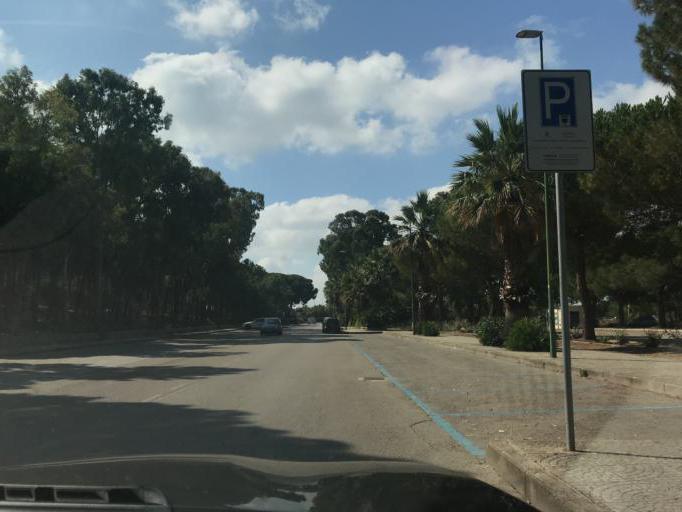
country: IT
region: Sardinia
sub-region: Provincia di Sassari
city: Alghero
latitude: 40.5845
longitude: 8.3102
